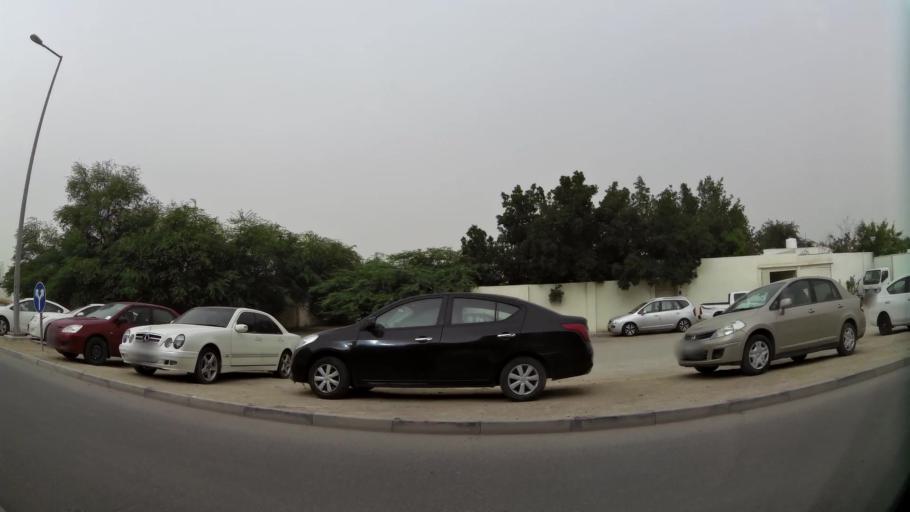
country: QA
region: Baladiyat ad Dawhah
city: Doha
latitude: 25.2558
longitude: 51.4952
